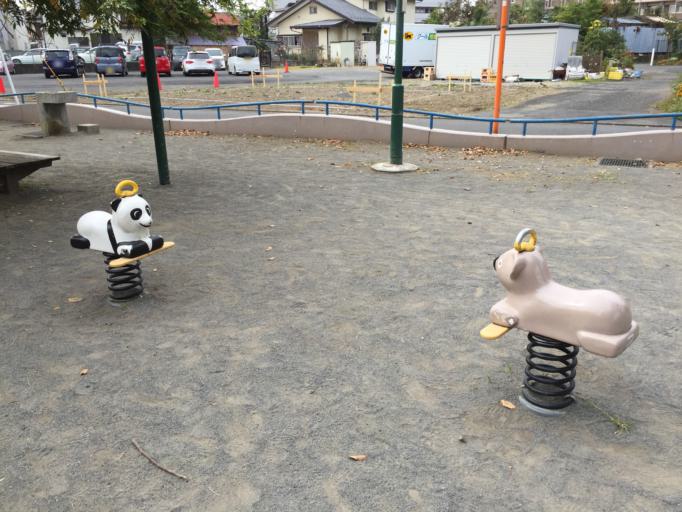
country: JP
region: Tokyo
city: Chofugaoka
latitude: 35.6626
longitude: 139.5027
